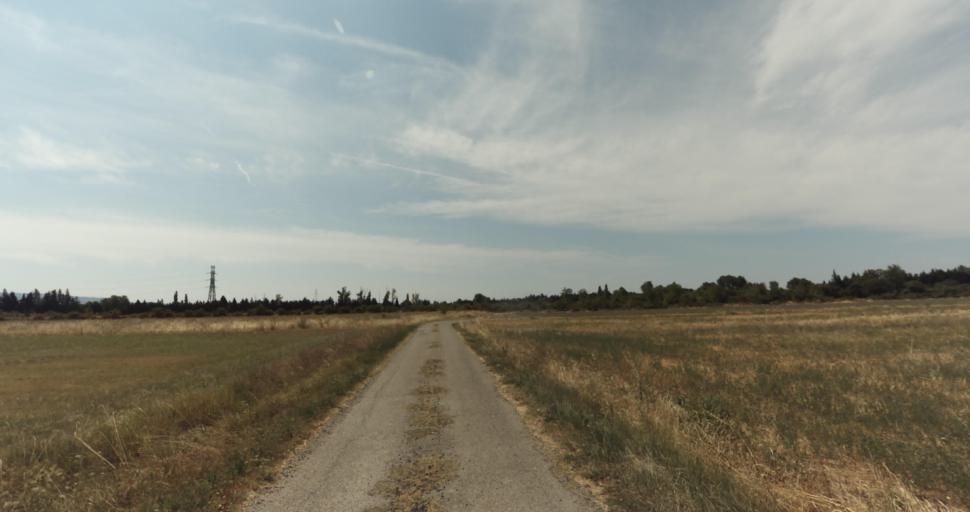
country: FR
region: Provence-Alpes-Cote d'Azur
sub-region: Departement du Vaucluse
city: Monteux
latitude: 44.0215
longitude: 4.9811
